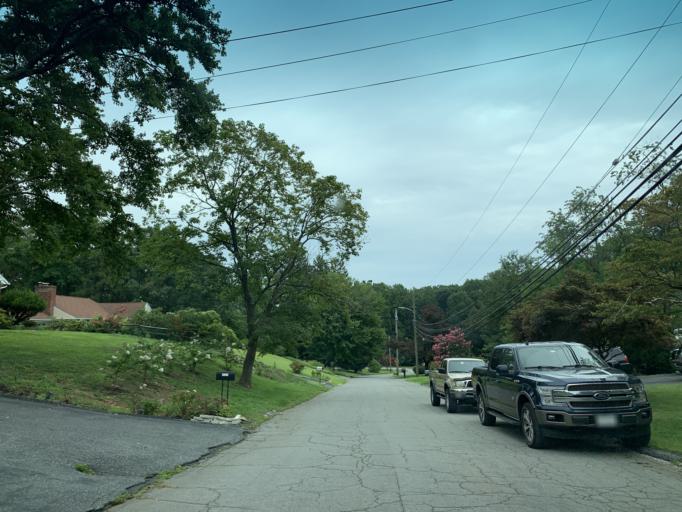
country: US
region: Maryland
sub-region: Baltimore County
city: Carney
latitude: 39.4078
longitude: -76.5235
